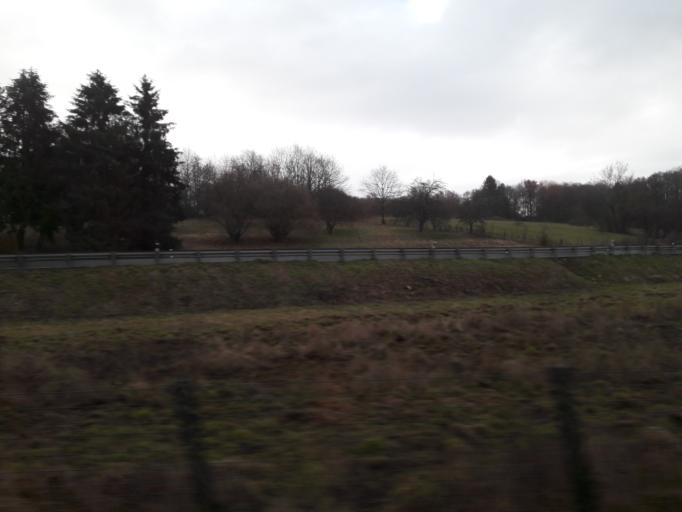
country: FR
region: Franche-Comte
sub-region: Territoire de Belfort
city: Morvillars
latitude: 47.5515
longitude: 6.9281
